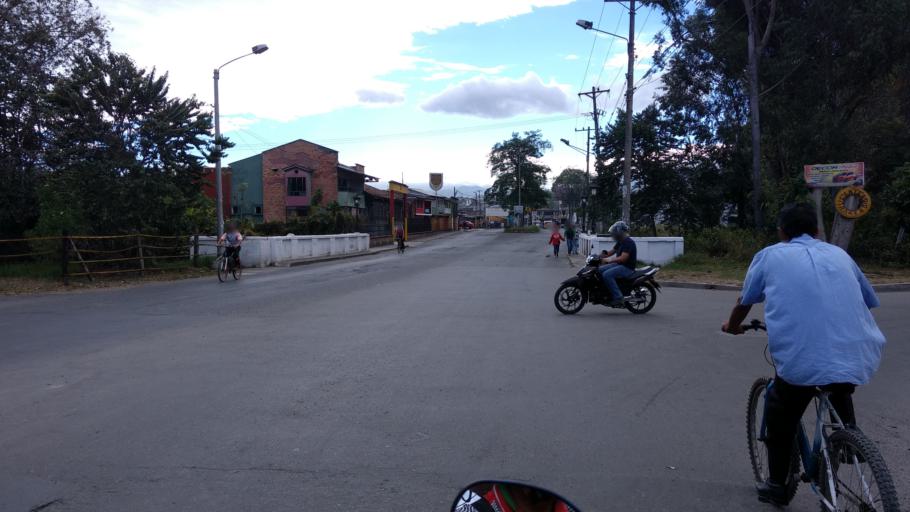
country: CO
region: Cauca
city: Popayan
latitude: 2.4462
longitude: -76.6105
